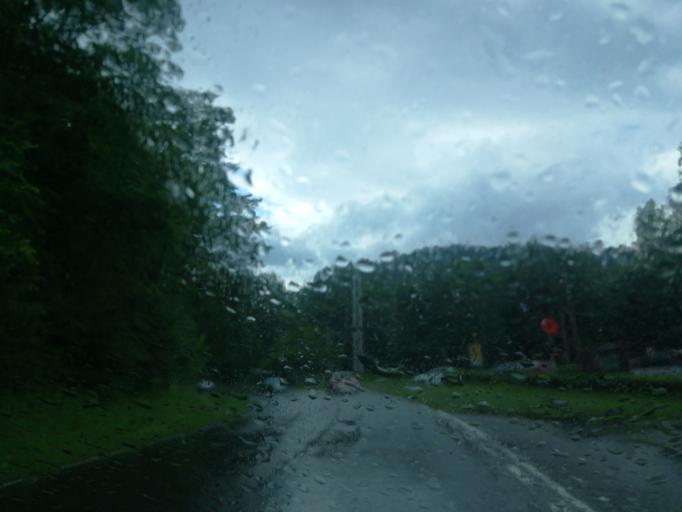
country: PL
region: Subcarpathian Voivodeship
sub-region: Powiat leski
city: Polanczyk
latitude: 49.4031
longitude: 22.4588
